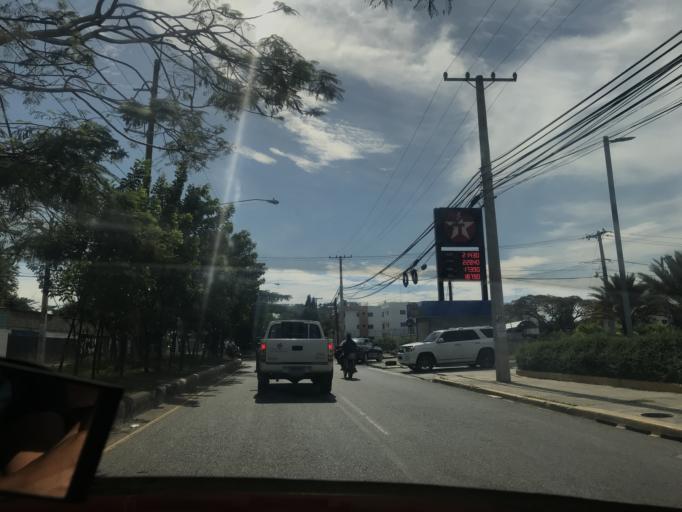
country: DO
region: Santiago
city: Santiago de los Caballeros
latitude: 19.4406
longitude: -70.7257
